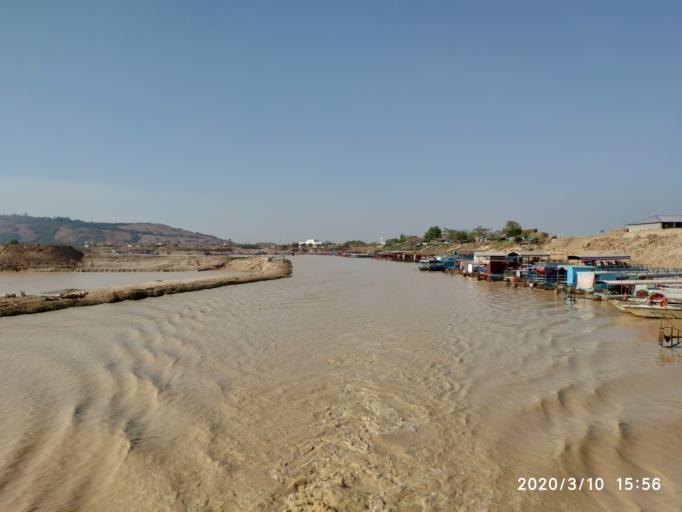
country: KH
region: Siem Reap
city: Siem Reap
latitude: 13.2666
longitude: 103.8214
